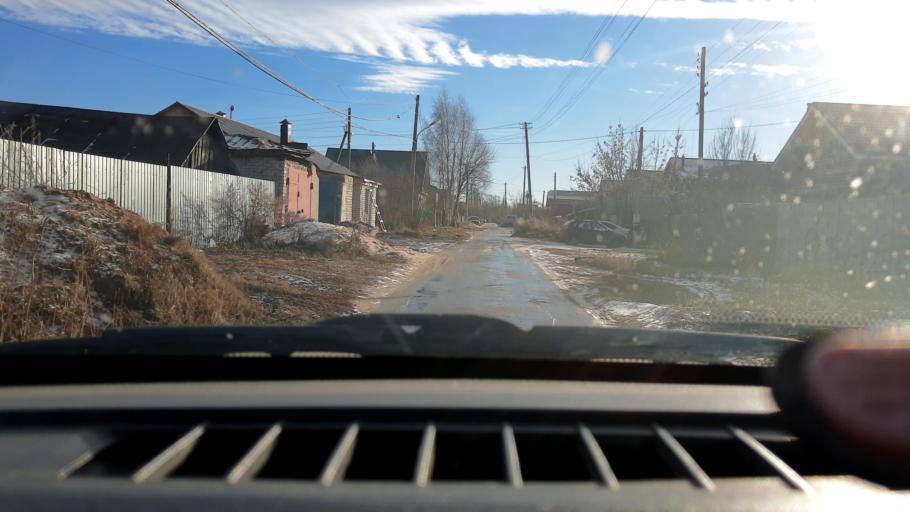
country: RU
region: Nizjnij Novgorod
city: Gorbatovka
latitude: 56.2985
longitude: 43.8453
